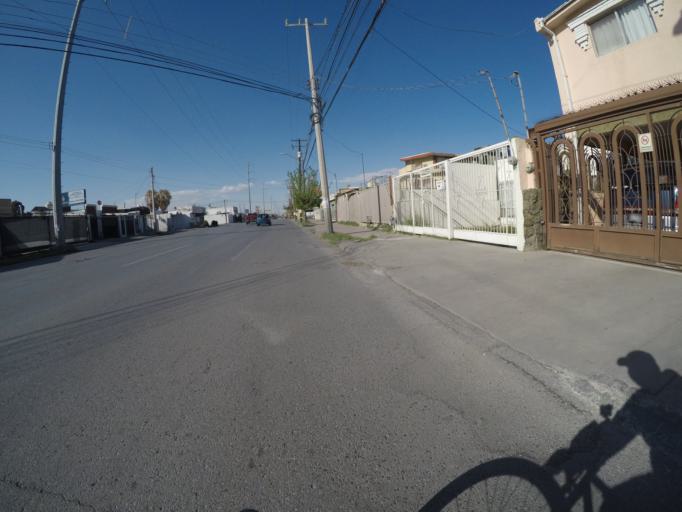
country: MX
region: Chihuahua
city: Ciudad Juarez
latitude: 31.7259
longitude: -106.4421
